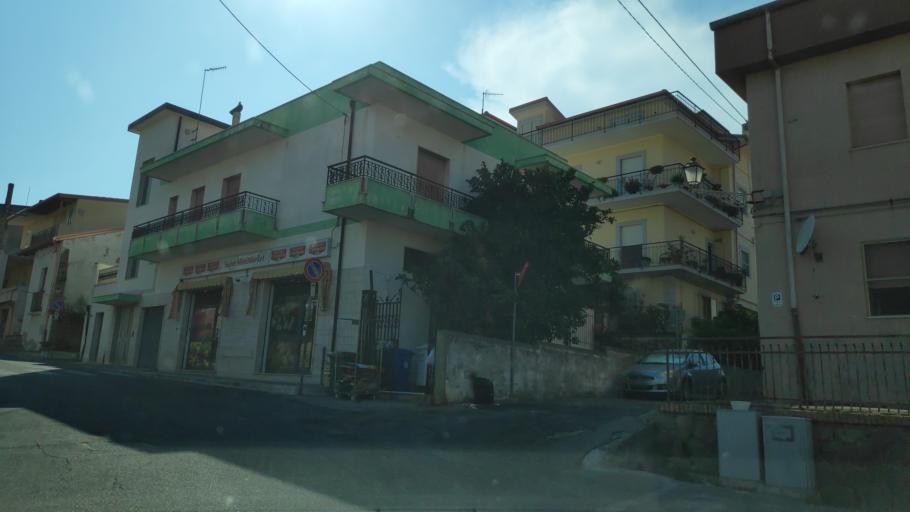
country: IT
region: Calabria
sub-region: Provincia di Catanzaro
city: Soverato Superiore
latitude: 38.6898
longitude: 16.5322
